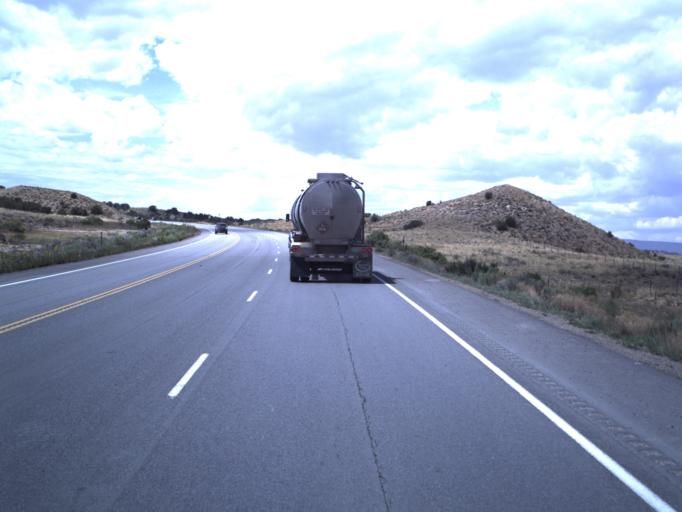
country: US
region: Utah
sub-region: Duchesne County
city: Duchesne
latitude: 40.1649
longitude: -110.4201
